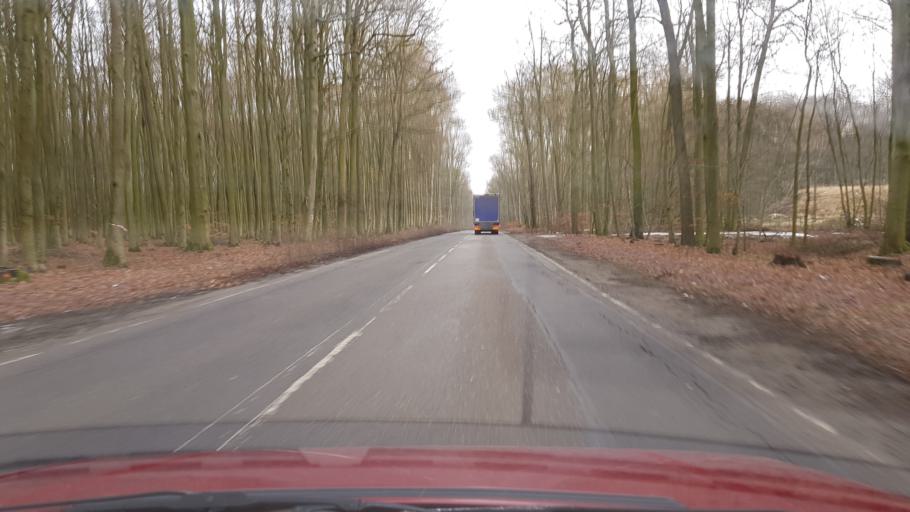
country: PL
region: West Pomeranian Voivodeship
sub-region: Powiat policki
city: Police
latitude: 53.5280
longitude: 14.5715
